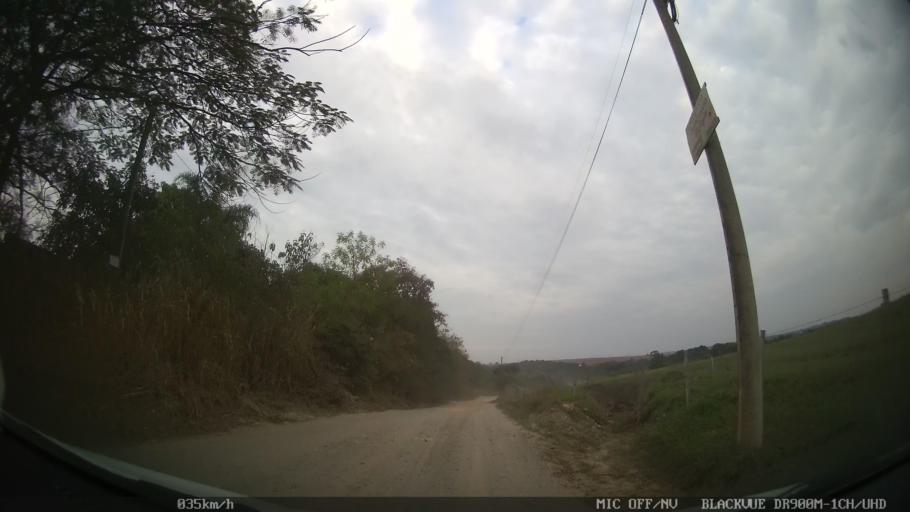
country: BR
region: Sao Paulo
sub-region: Santa Barbara D'Oeste
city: Santa Barbara d'Oeste
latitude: -22.6906
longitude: -47.3874
